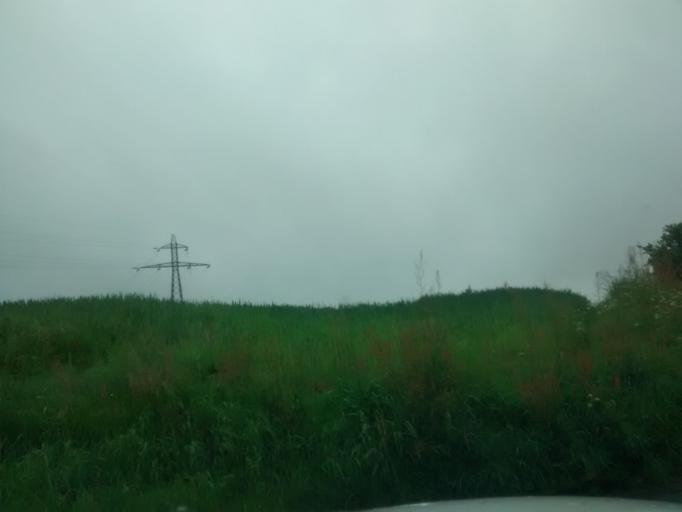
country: FR
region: Brittany
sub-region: Departement d'Ille-et-Vilaine
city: Noyal-sur-Vilaine
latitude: 48.0993
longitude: -1.5562
